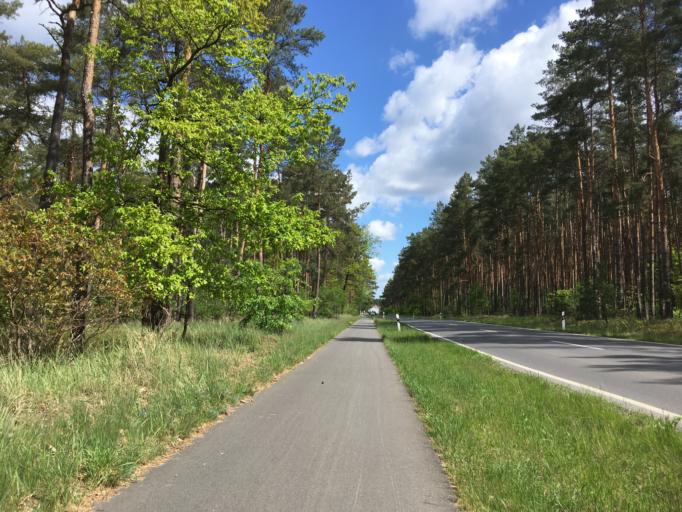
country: DE
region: Brandenburg
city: Oranienburg
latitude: 52.7845
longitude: 13.2641
